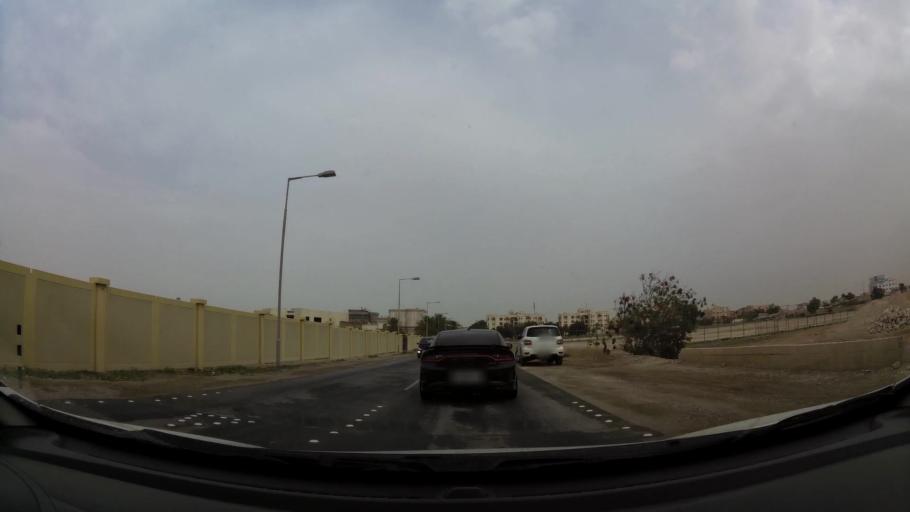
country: BH
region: Northern
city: Ar Rifa'
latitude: 26.1326
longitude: 50.5481
